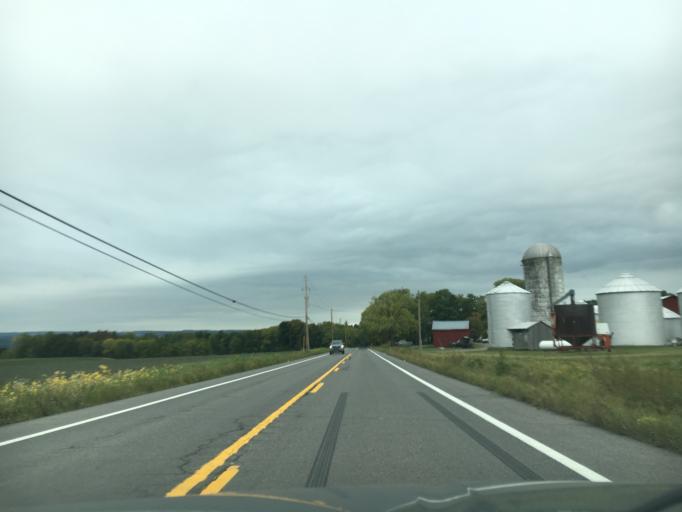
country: US
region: New York
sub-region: Tompkins County
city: Trumansburg
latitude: 42.6711
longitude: -76.7357
